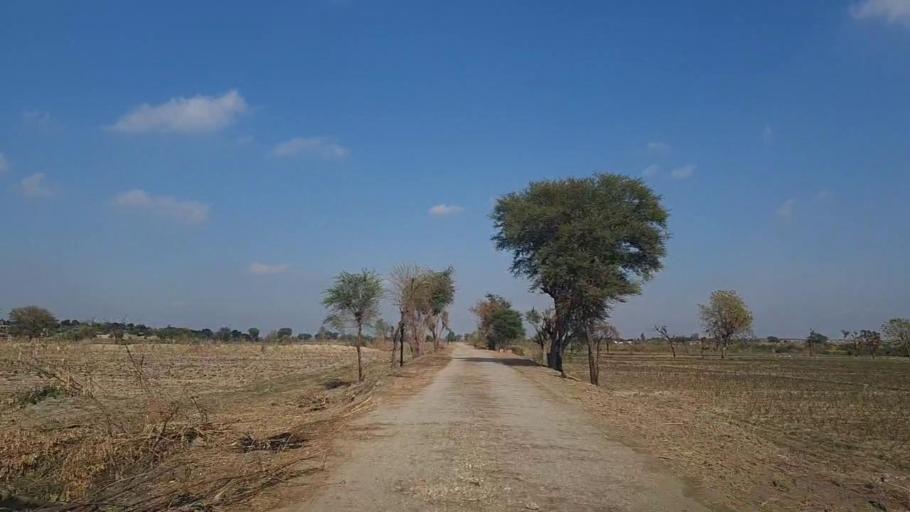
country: PK
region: Sindh
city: Tando Mittha Khan
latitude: 25.9884
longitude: 69.2405
